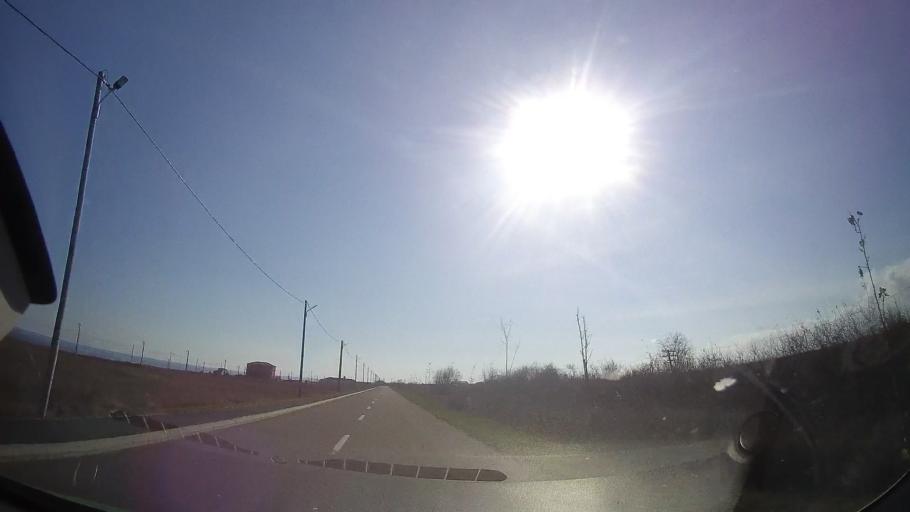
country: RO
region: Constanta
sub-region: Comuna Costinesti
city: Schitu
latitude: 43.9308
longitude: 28.6315
